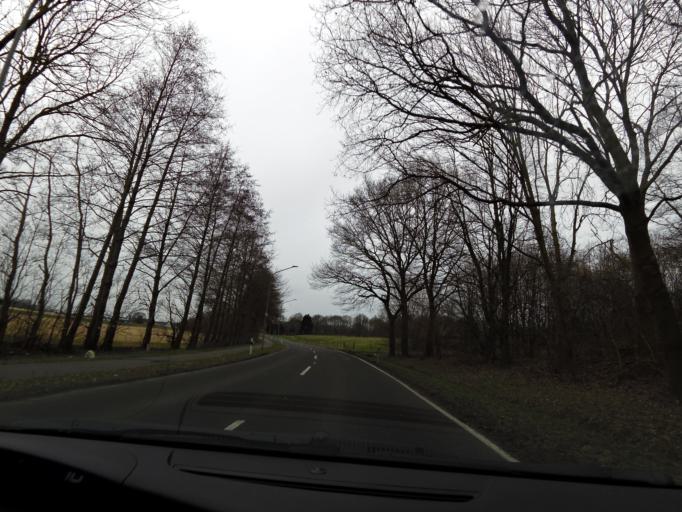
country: DE
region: North Rhine-Westphalia
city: Geilenkirchen
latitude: 50.9734
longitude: 6.0792
